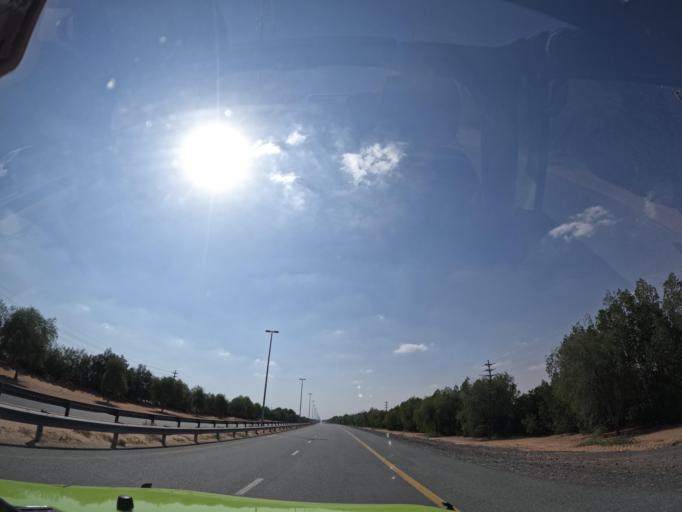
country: AE
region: Ash Shariqah
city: Adh Dhayd
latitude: 24.9011
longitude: 55.7775
